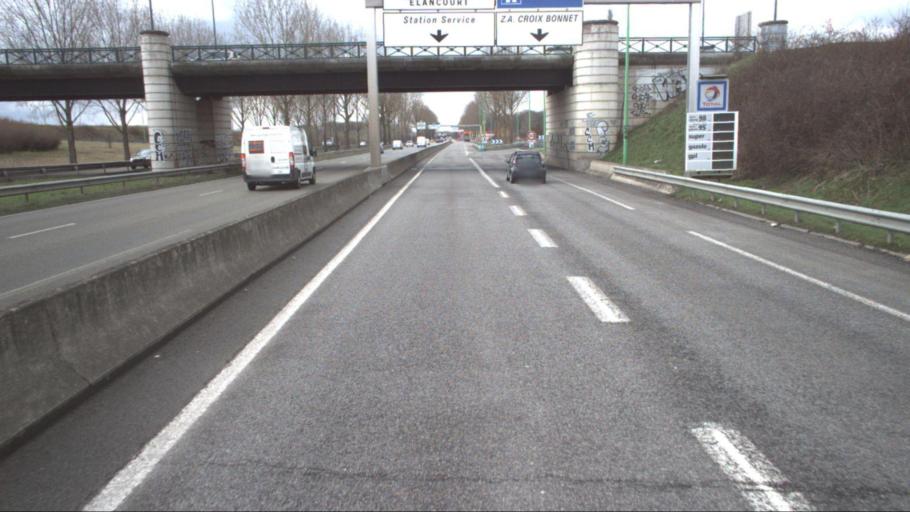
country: FR
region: Ile-de-France
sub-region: Departement des Yvelines
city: Bois-d'Arcy
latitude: 48.7980
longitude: 2.0111
